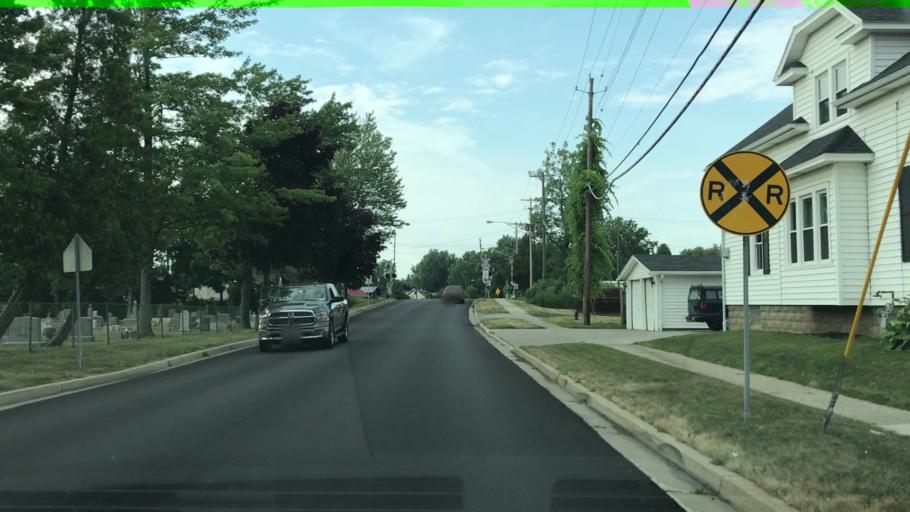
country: US
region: New York
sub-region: Erie County
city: Lancaster
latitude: 42.9041
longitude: -78.6732
